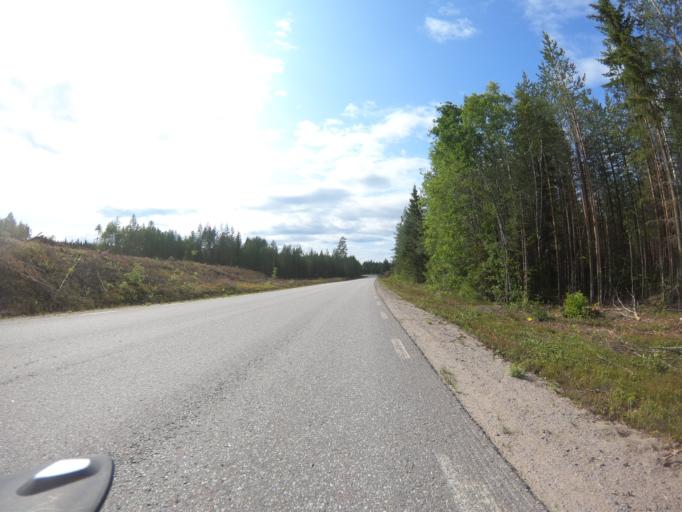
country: SE
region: Vaesterbotten
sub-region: Umea Kommun
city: Roback
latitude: 63.8262
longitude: 20.1496
